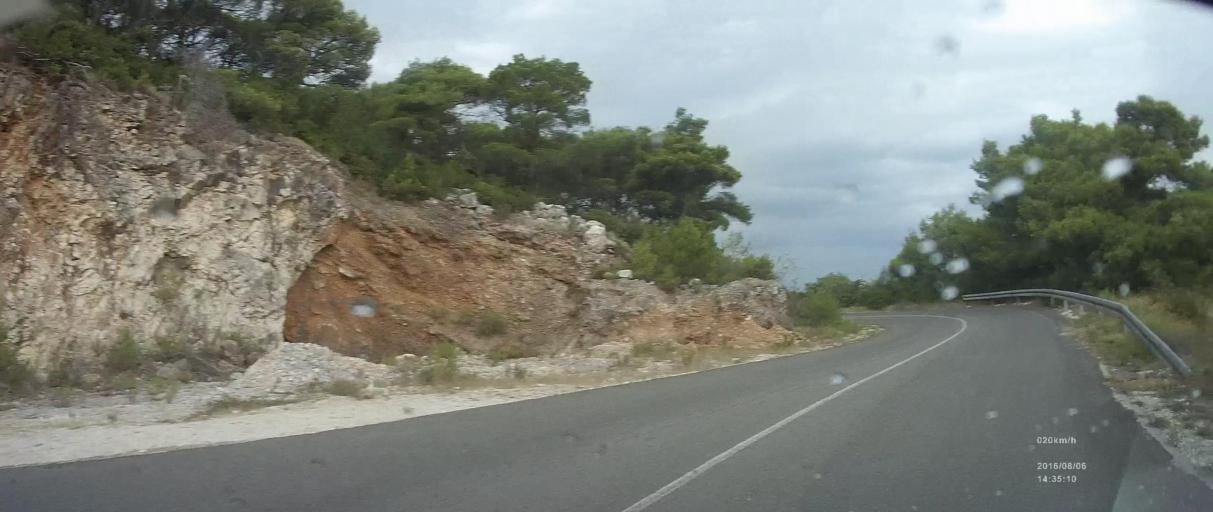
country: HR
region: Dubrovacko-Neretvanska
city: Ston
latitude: 42.7101
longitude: 17.6941
